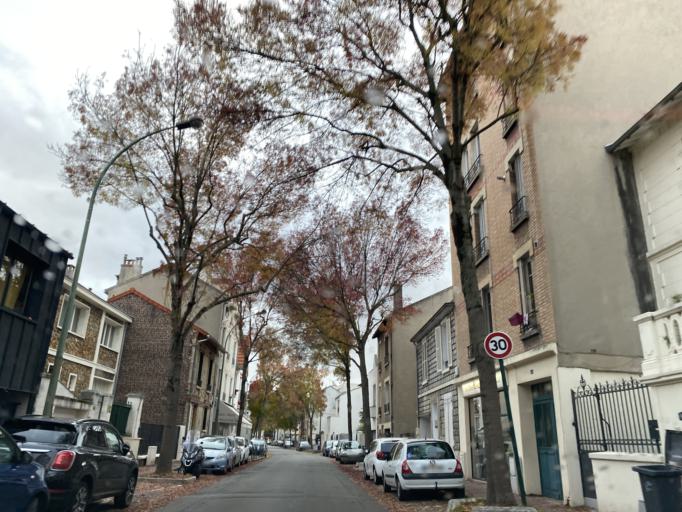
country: FR
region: Ile-de-France
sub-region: Departement des Hauts-de-Seine
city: Suresnes
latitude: 48.8628
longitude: 2.2224
